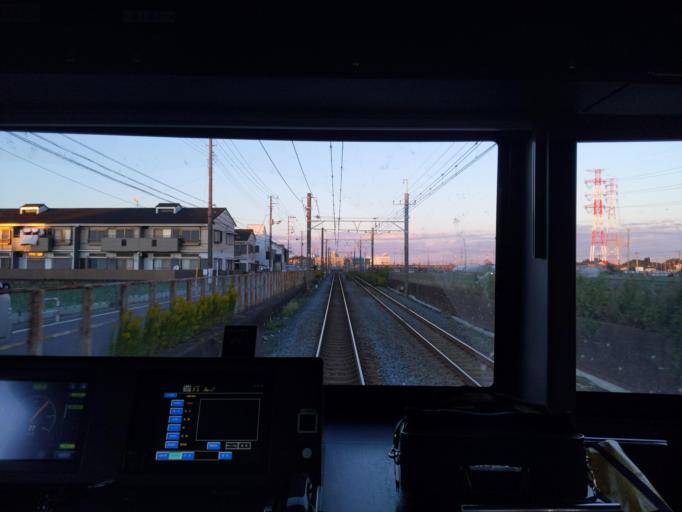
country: JP
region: Chiba
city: Funabashi
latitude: 35.7291
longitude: 139.9886
